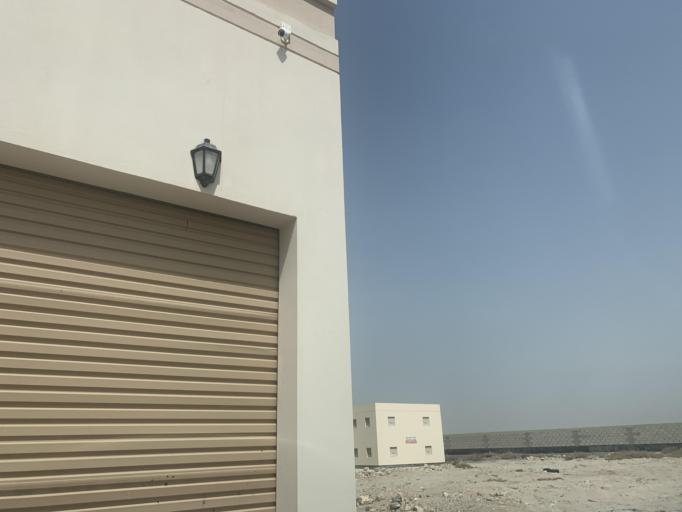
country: BH
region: Northern
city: Madinat `Isa
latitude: 26.1851
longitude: 50.4901
